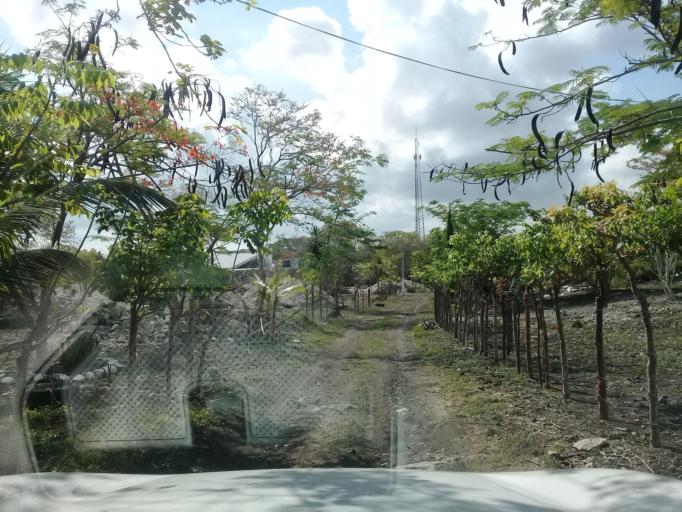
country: MX
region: Veracruz
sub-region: Emiliano Zapata
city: Plan del Rio
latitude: 19.4117
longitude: -96.6539
